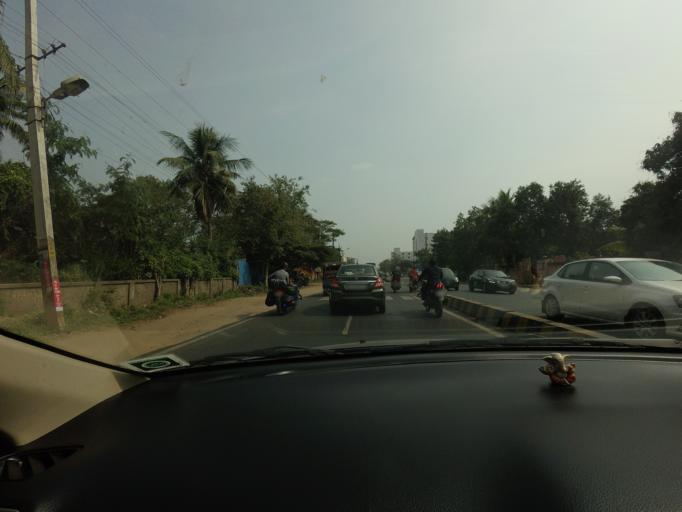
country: IN
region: Andhra Pradesh
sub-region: Krishna
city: Yanamalakuduru
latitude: 16.4891
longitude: 80.6740
